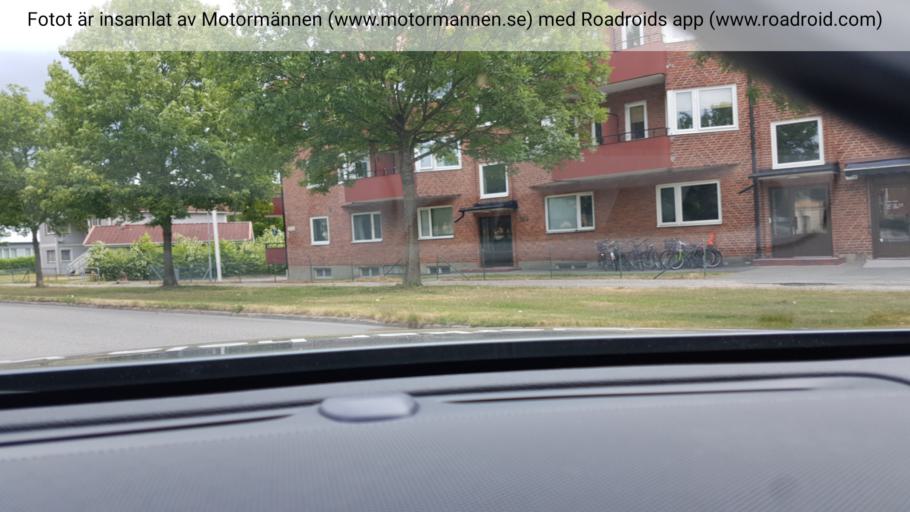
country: SE
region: Skane
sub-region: Hassleholms Kommun
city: Hassleholm
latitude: 56.1645
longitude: 13.7581
